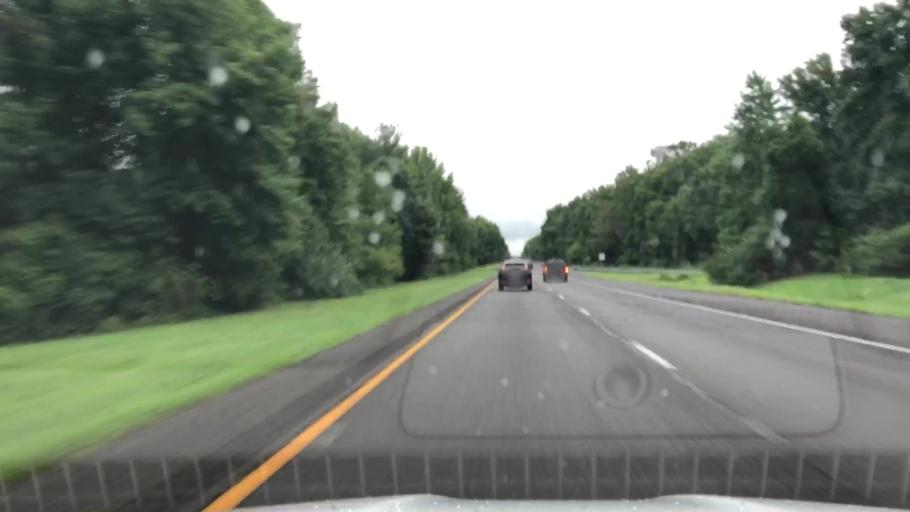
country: US
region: New Jersey
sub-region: Salem County
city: Carneys Point
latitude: 39.7098
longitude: -75.4440
